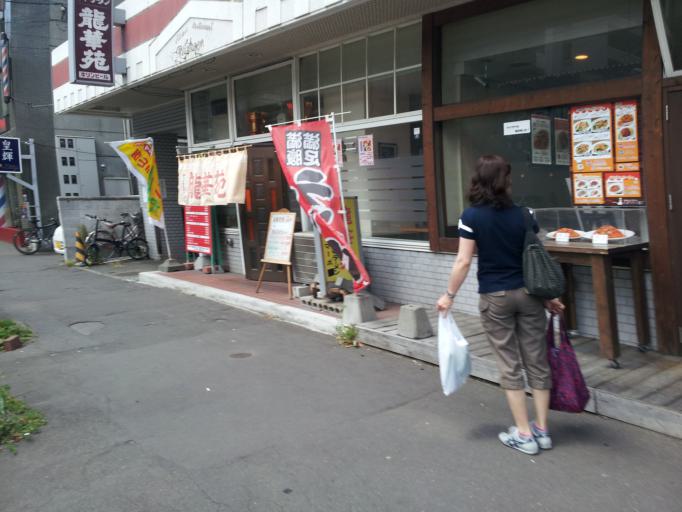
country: JP
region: Hokkaido
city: Sapporo
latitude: 43.0759
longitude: 141.3483
